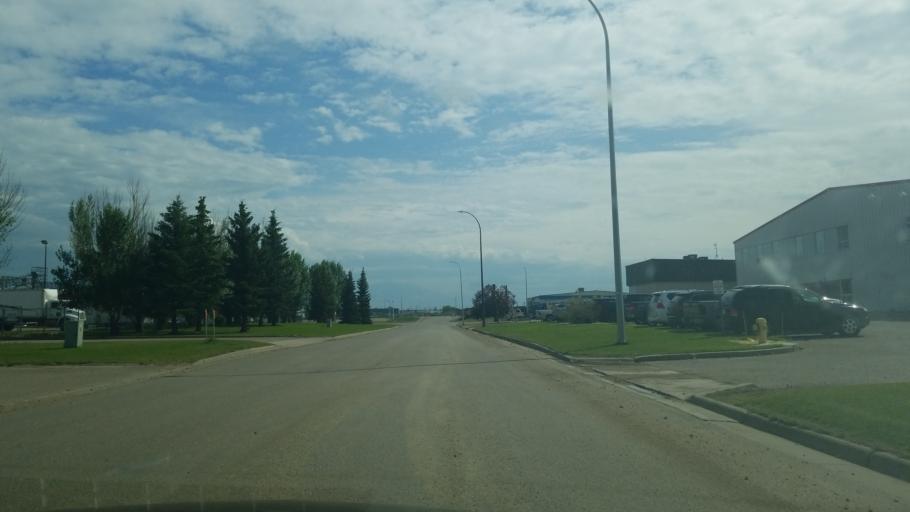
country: CA
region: Saskatchewan
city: Lloydminster
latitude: 53.2882
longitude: -110.0368
